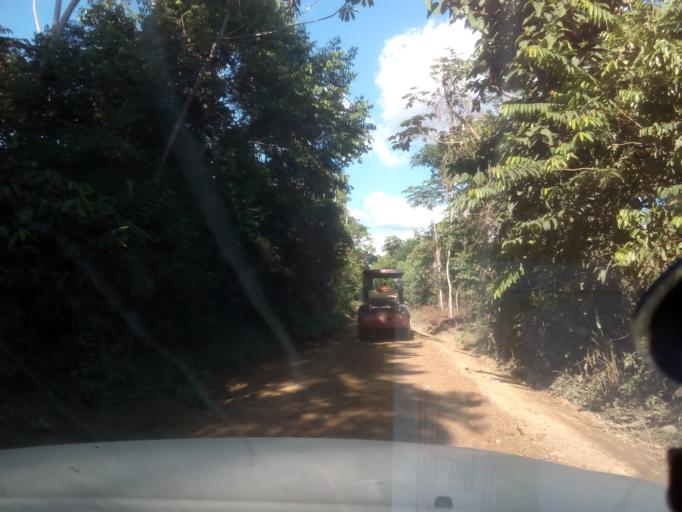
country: PE
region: Cusco
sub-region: Provincia de Quispicanchis
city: Quince Mil
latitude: -12.6402
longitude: -70.3711
